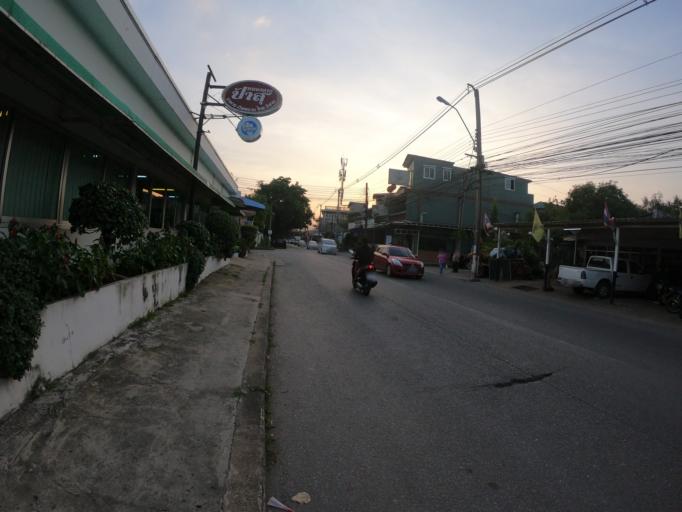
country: TH
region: Bangkok
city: Lat Phrao
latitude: 13.8307
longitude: 100.6094
